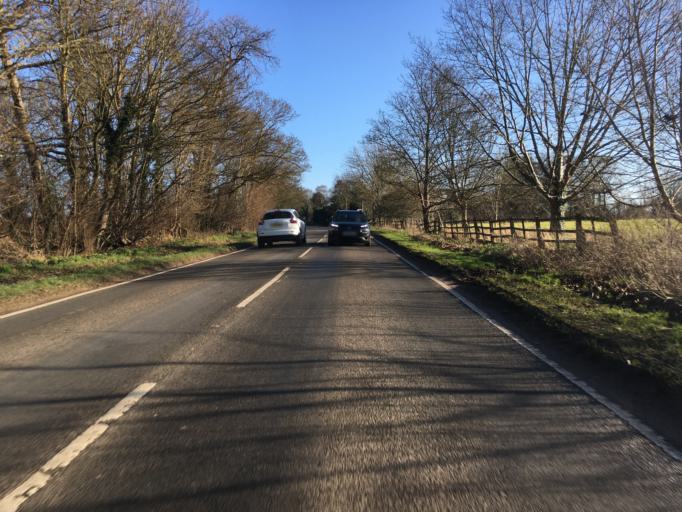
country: GB
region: England
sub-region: Warwickshire
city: Stratford-upon-Avon
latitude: 52.2027
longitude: -1.6556
